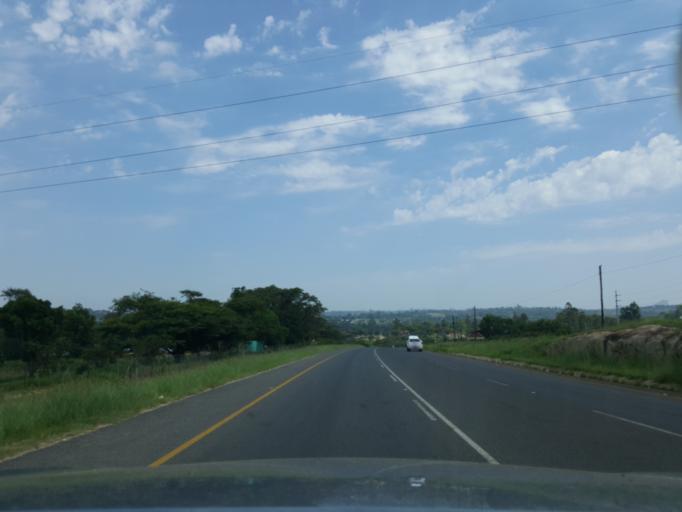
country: ZA
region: Mpumalanga
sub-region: Ehlanzeni District
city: White River
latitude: -25.3618
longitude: 31.0723
